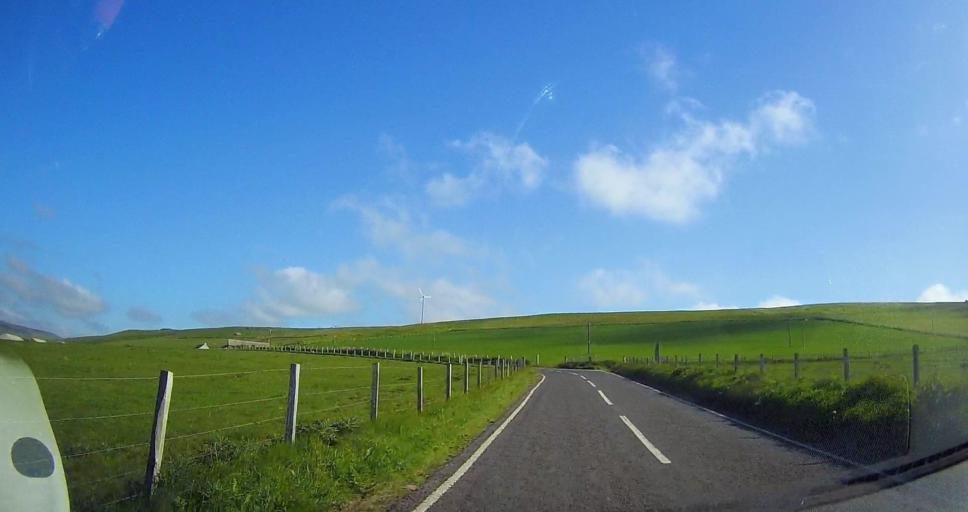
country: GB
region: Scotland
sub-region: Orkney Islands
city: Stromness
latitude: 59.1182
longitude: -3.3058
